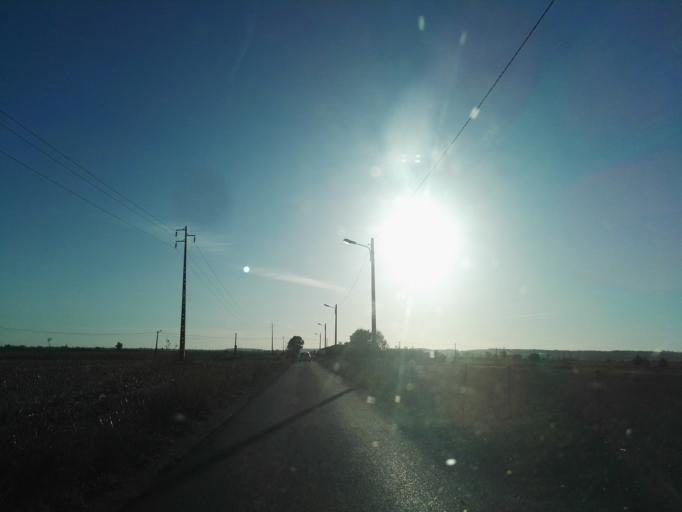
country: PT
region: Santarem
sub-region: Golega
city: Golega
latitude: 39.4053
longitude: -8.4964
